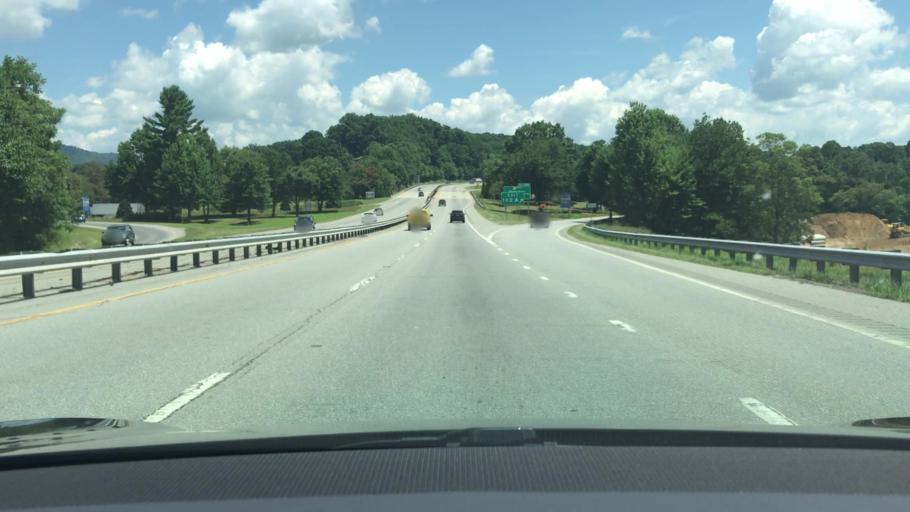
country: US
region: North Carolina
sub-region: Haywood County
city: Waynesville
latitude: 35.5045
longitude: -82.9951
